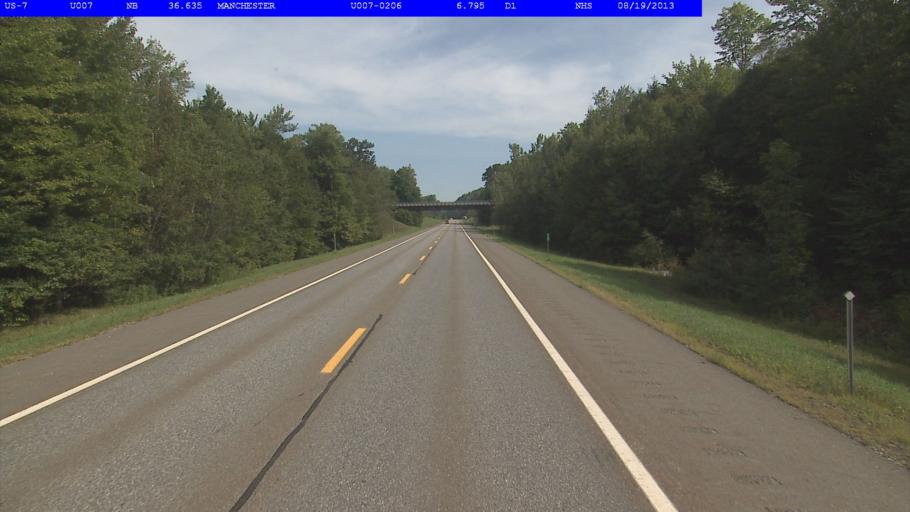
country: US
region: Vermont
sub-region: Bennington County
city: Manchester Center
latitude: 43.2003
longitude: -73.0117
